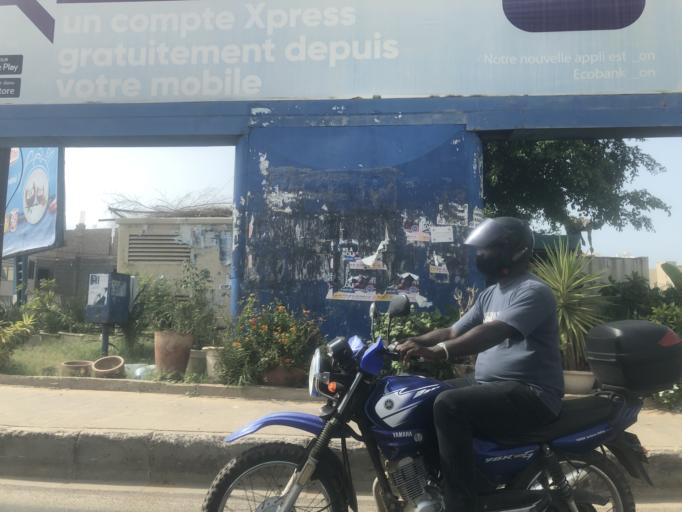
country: SN
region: Dakar
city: Mermoz Boabab
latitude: 14.7438
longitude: -17.5118
